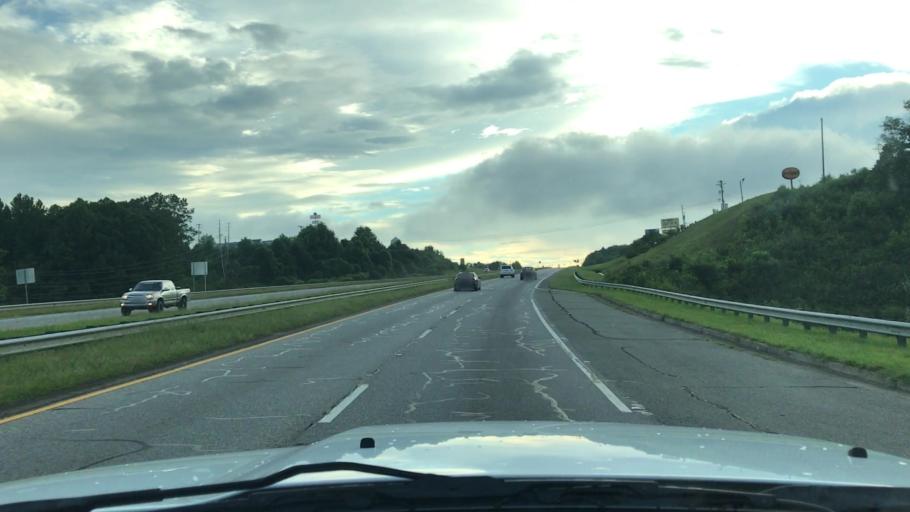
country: US
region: Georgia
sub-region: Fannin County
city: Blue Ridge
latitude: 34.8759
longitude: -84.3028
